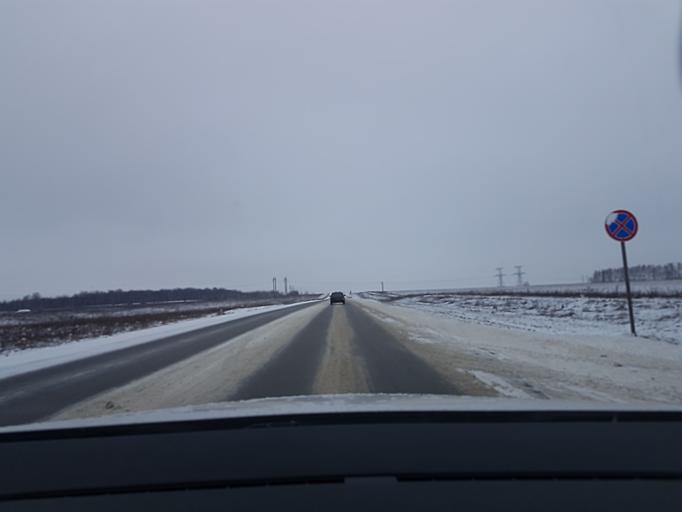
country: RU
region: Rjazan
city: Skopin
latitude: 53.9583
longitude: 39.4299
